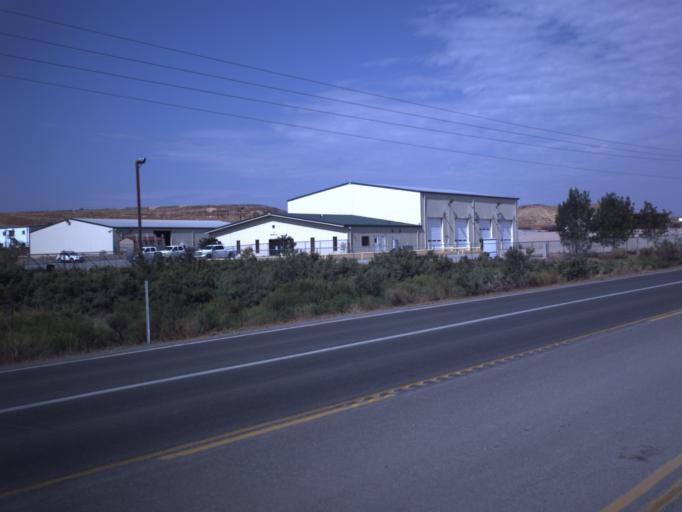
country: US
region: Utah
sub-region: Uintah County
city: Naples
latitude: 40.3892
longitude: -109.4407
